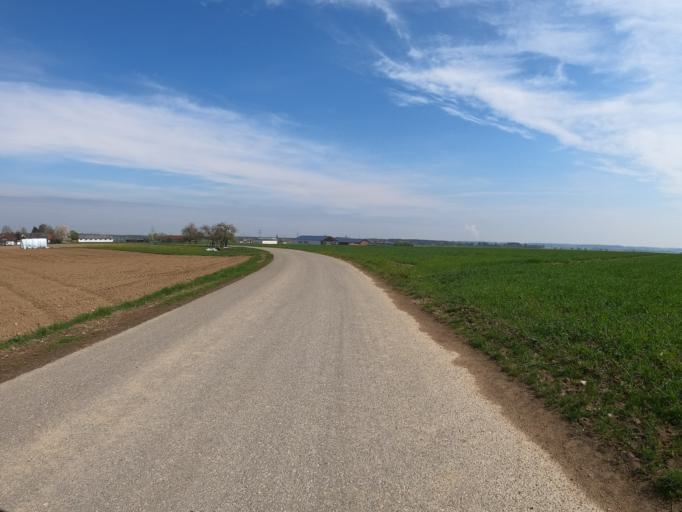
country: DE
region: Bavaria
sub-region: Swabia
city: Rieden an der Kotz
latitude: 48.3790
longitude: 10.2186
